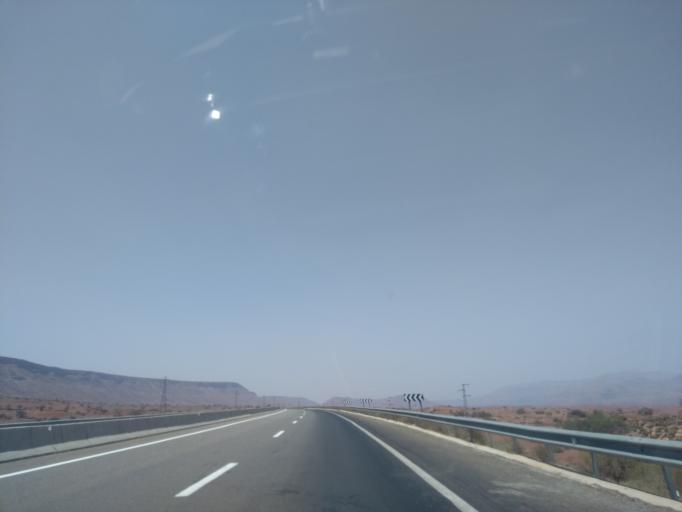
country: MA
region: Marrakech-Tensift-Al Haouz
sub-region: Chichaoua
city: Timezgadiouine
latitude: 30.8809
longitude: -9.0793
